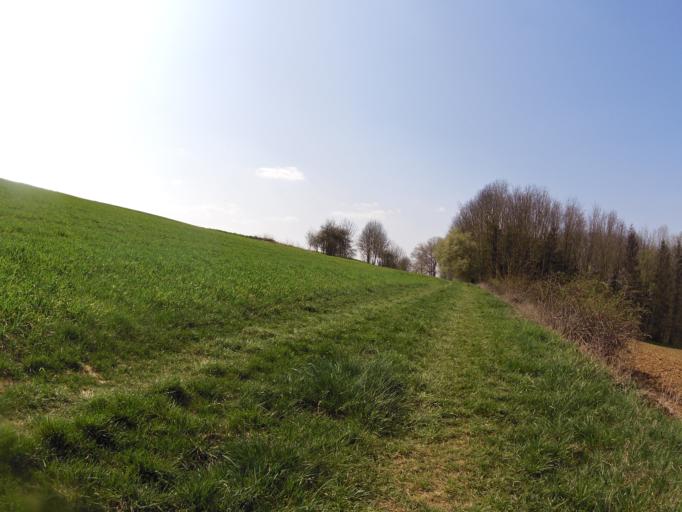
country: DE
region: Bavaria
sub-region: Regierungsbezirk Unterfranken
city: Dettelbach
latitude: 49.8203
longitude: 10.1407
